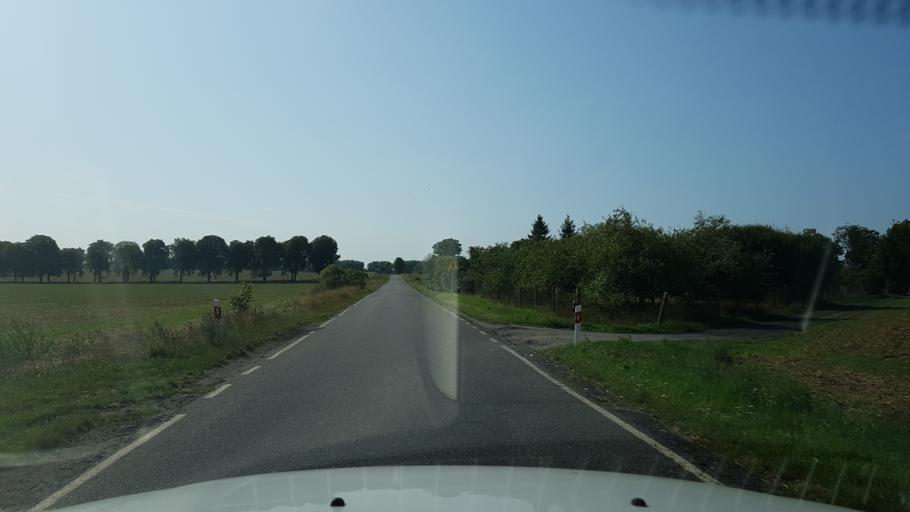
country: PL
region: West Pomeranian Voivodeship
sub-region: Powiat stargardzki
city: Dolice
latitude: 53.1473
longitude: 15.2421
